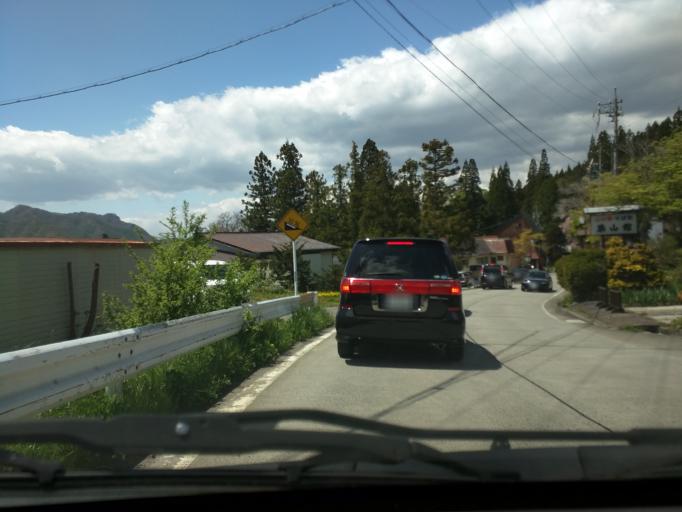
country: JP
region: Nagano
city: Nagano-shi
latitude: 36.7312
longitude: 138.0787
